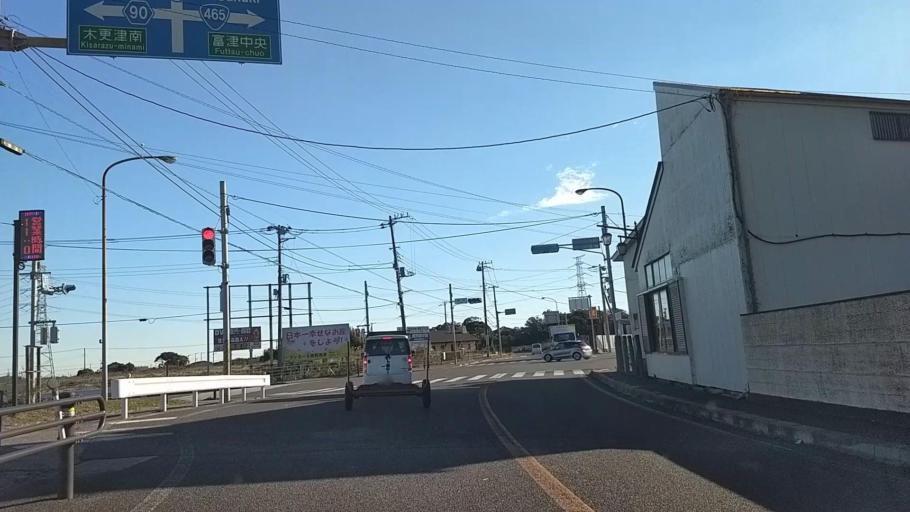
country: JP
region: Chiba
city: Futtsu
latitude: 35.3152
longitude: 139.8255
